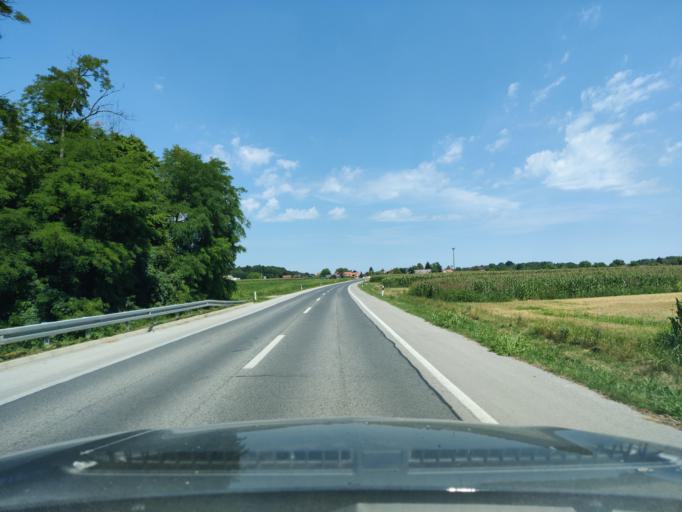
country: HR
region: Medimurska
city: Mackovec
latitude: 46.4186
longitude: 16.4255
